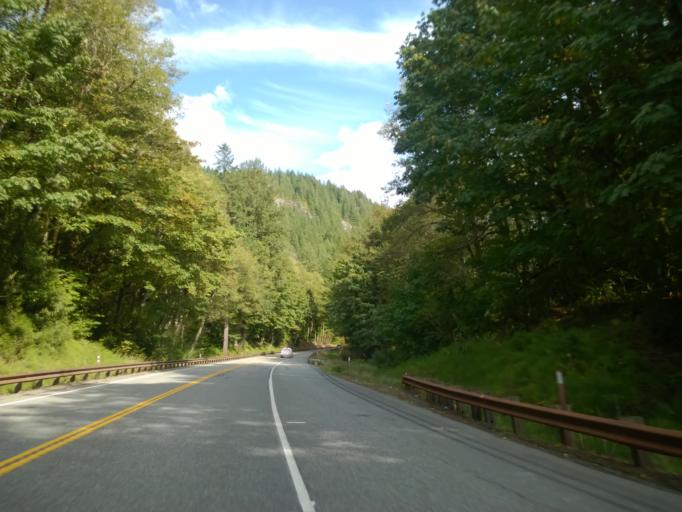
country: US
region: Washington
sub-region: Snohomish County
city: Gold Bar
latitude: 47.7172
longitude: -121.2788
